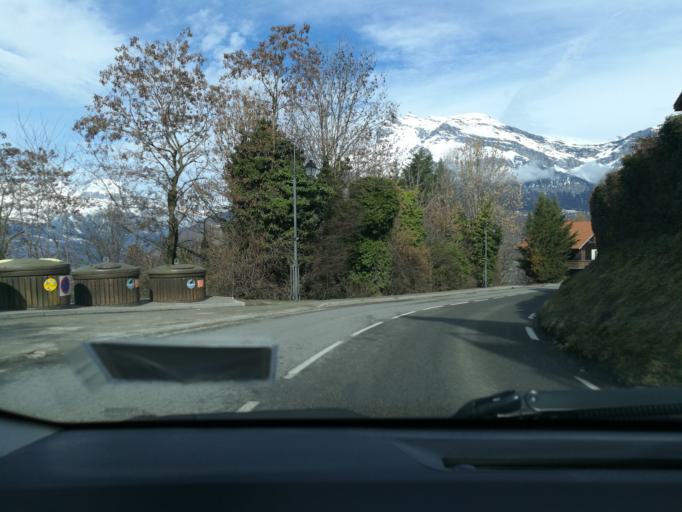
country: FR
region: Rhone-Alpes
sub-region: Departement de la Haute-Savoie
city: Saint-Gervais-les-Bains
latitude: 45.8972
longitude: 6.7091
